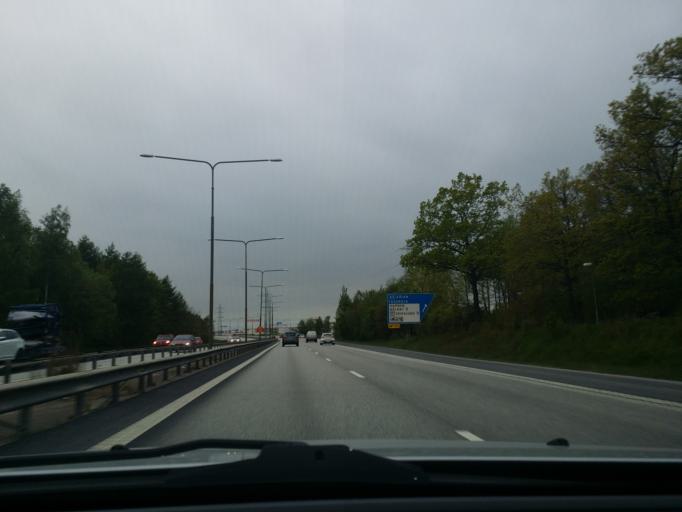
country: SE
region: Vaestmanland
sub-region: Vasteras
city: Vasteras
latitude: 59.6133
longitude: 16.4850
